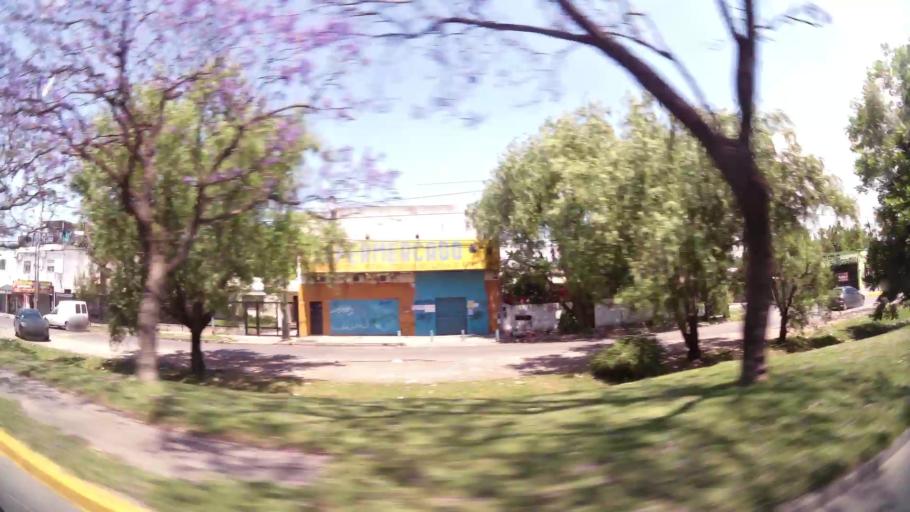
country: AR
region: Buenos Aires
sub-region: Partido de Tigre
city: Tigre
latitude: -34.4484
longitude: -58.6061
